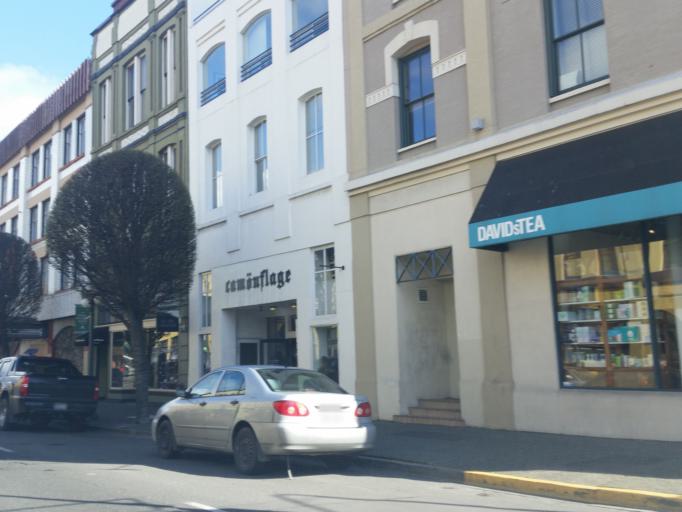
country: CA
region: British Columbia
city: Victoria
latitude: 48.4276
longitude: -123.3672
